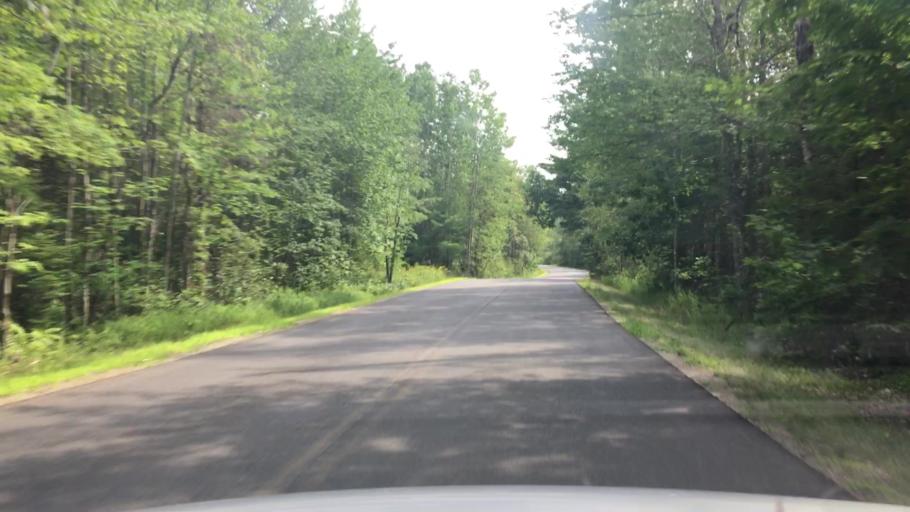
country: US
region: Maine
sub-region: Lincoln County
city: Jefferson
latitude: 44.2473
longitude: -69.4460
